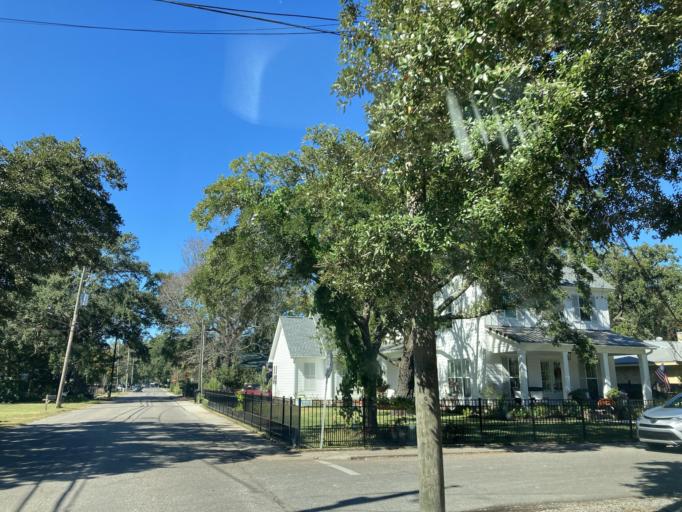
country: US
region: Mississippi
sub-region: Jackson County
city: Ocean Springs
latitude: 30.4114
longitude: -88.8211
